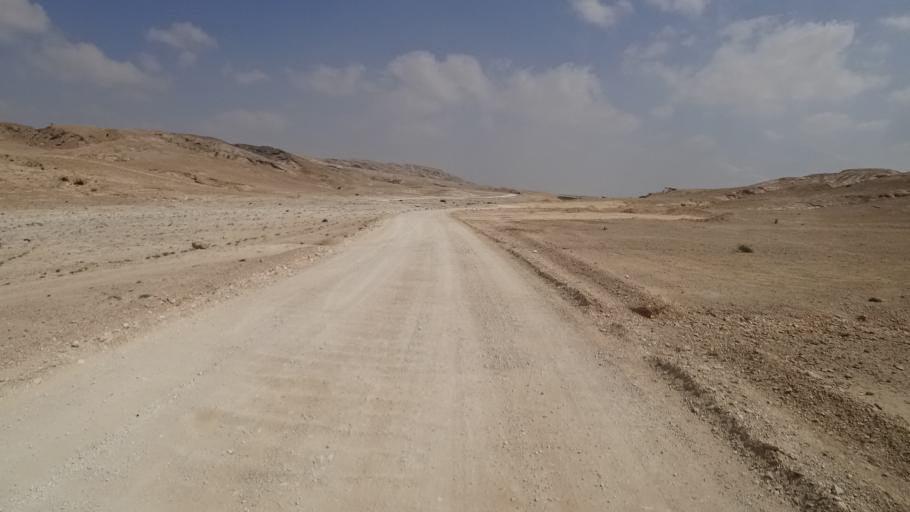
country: OM
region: Zufar
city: Salalah
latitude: 17.2407
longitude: 53.9061
